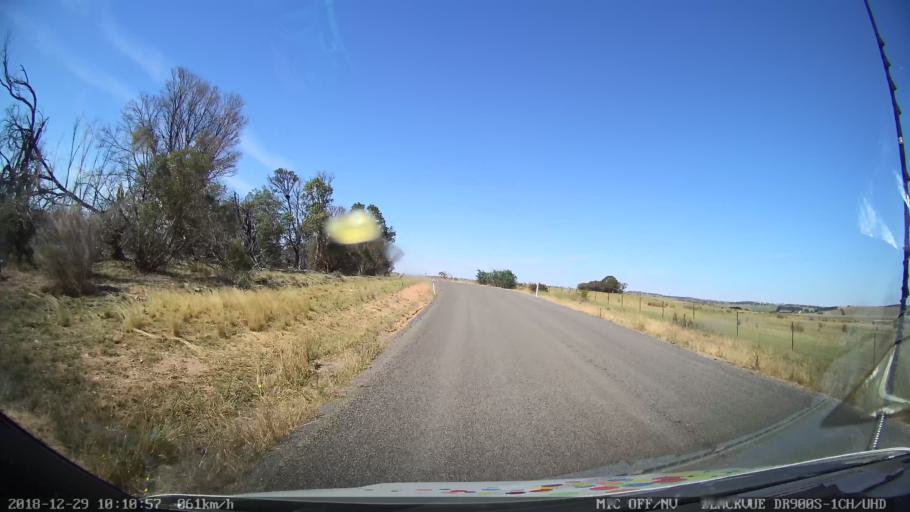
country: AU
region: New South Wales
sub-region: Yass Valley
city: Gundaroo
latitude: -34.8794
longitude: 149.4540
